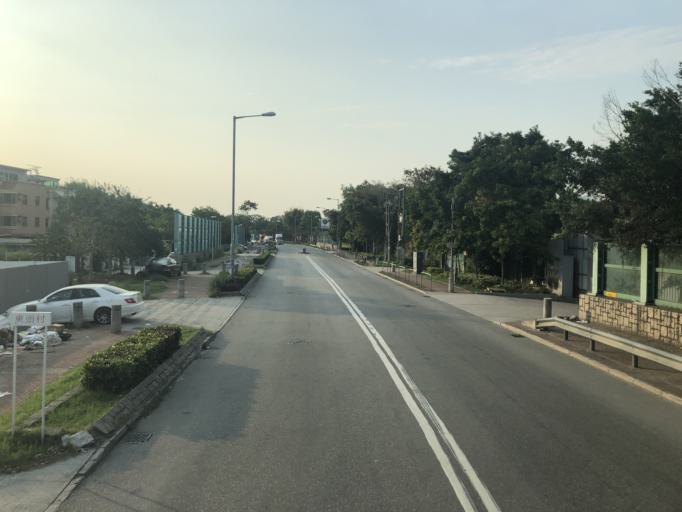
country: HK
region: Yuen Long
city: Yuen Long Kau Hui
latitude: 22.4534
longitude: 113.9946
